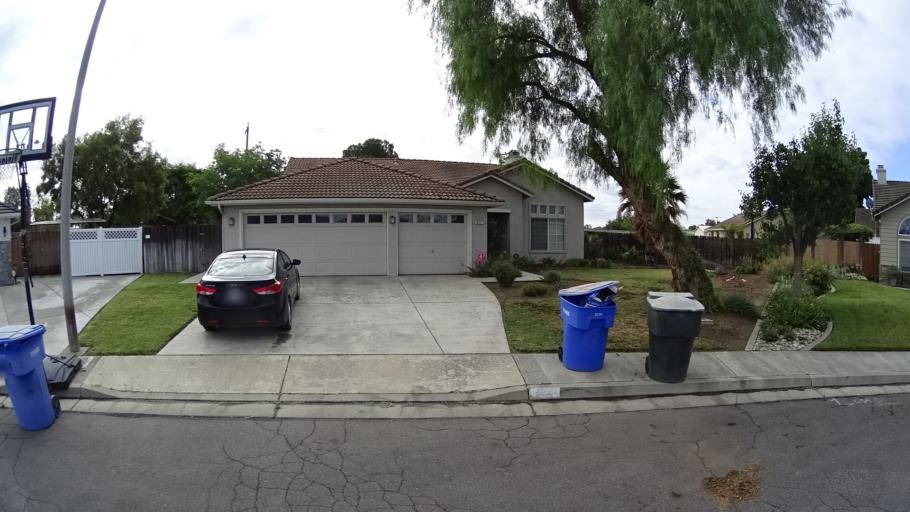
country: US
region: California
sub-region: Kings County
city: Hanford
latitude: 36.3594
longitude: -119.6318
